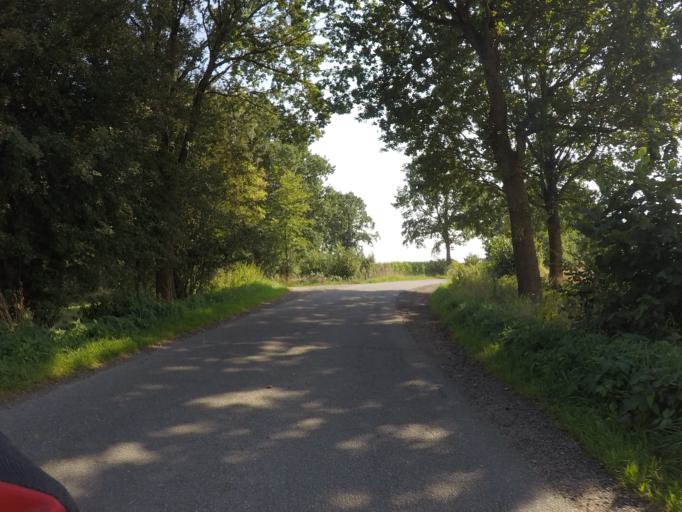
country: DE
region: Schleswig-Holstein
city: Seth
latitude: 53.8708
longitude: 10.1743
